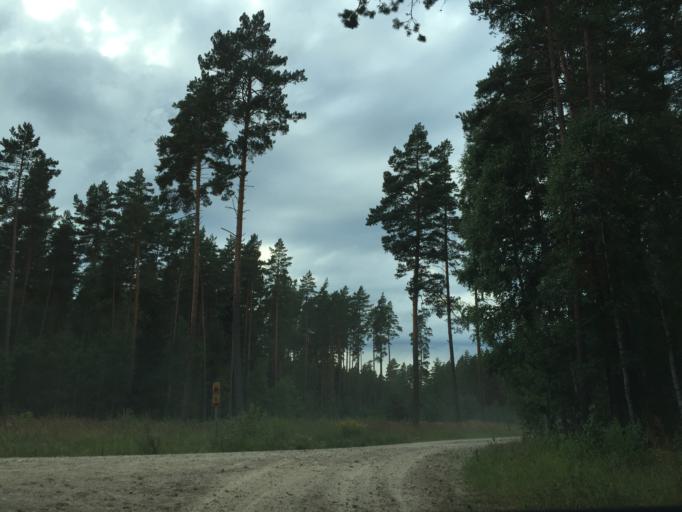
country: LV
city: Tireli
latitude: 56.8677
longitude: 23.6842
